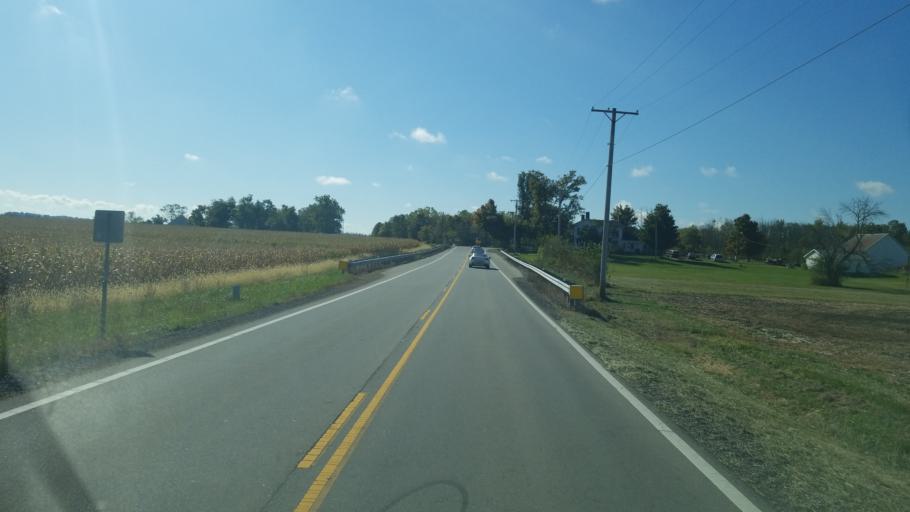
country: US
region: Ohio
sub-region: Fayette County
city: Washington Court House
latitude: 39.4585
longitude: -83.4896
